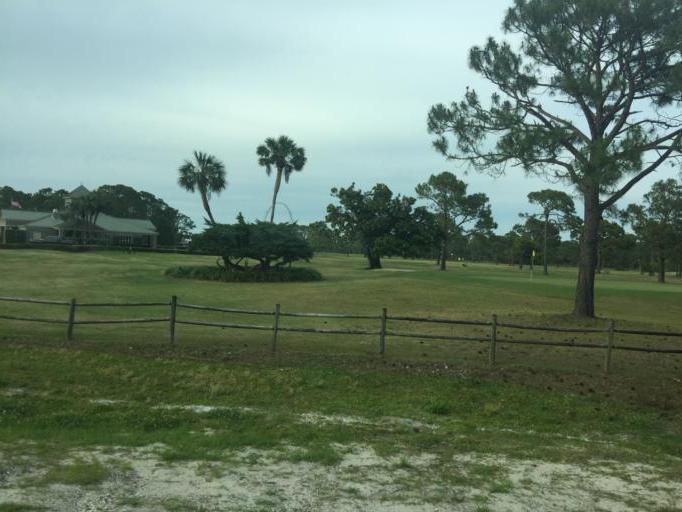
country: US
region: Florida
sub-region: Bay County
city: Panama City Beach
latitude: 30.1743
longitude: -85.7950
